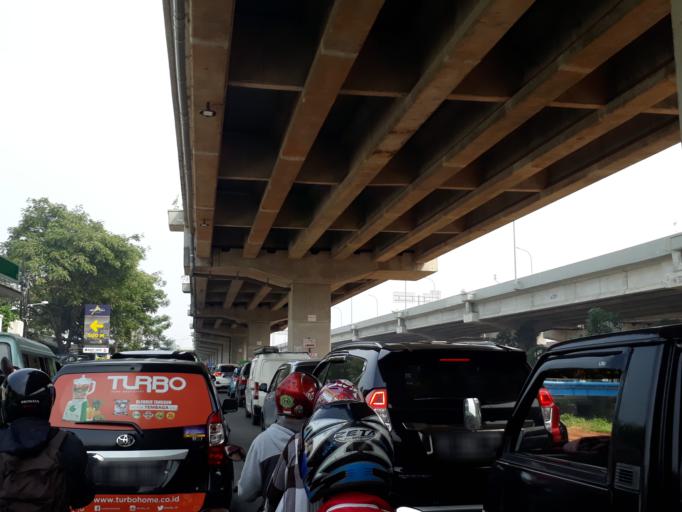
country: ID
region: West Java
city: Bekasi
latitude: -6.2489
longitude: 106.9304
